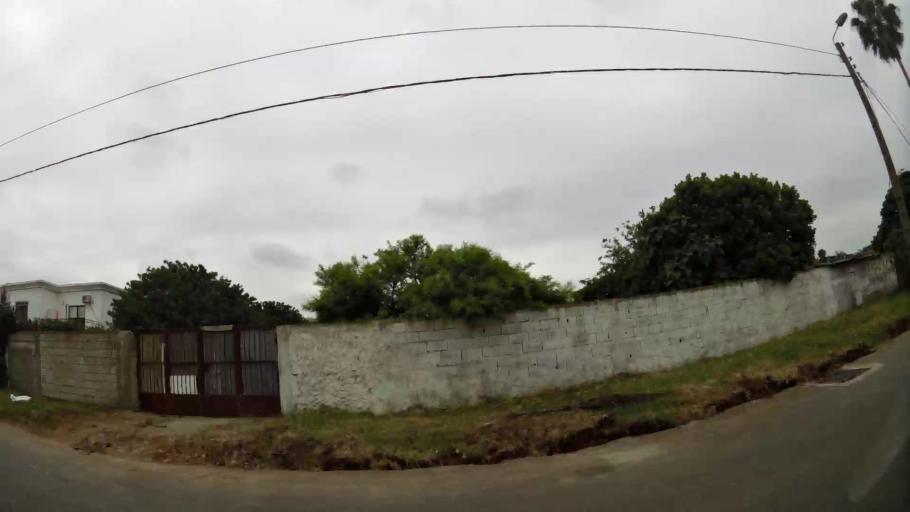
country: MA
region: Rabat-Sale-Zemmour-Zaer
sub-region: Rabat
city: Rabat
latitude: 33.9651
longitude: -6.8151
